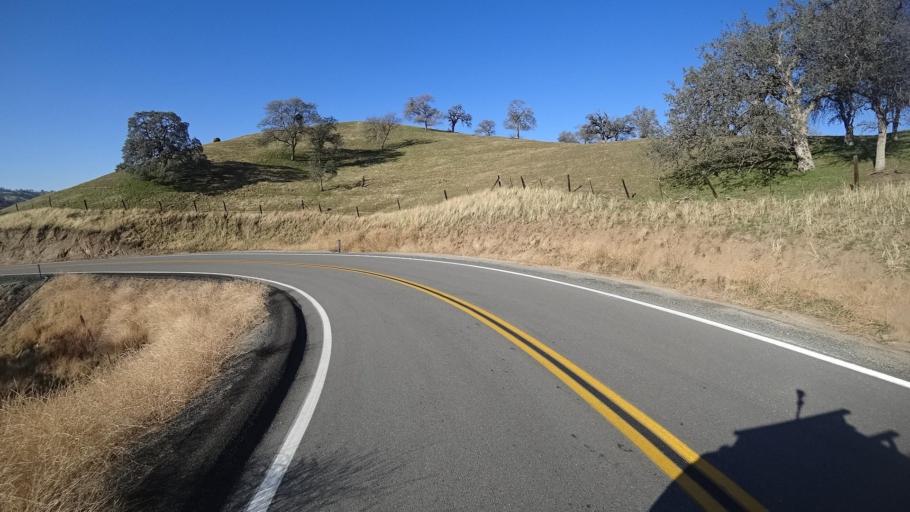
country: US
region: California
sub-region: Kern County
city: Alta Sierra
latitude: 35.7170
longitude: -118.8111
